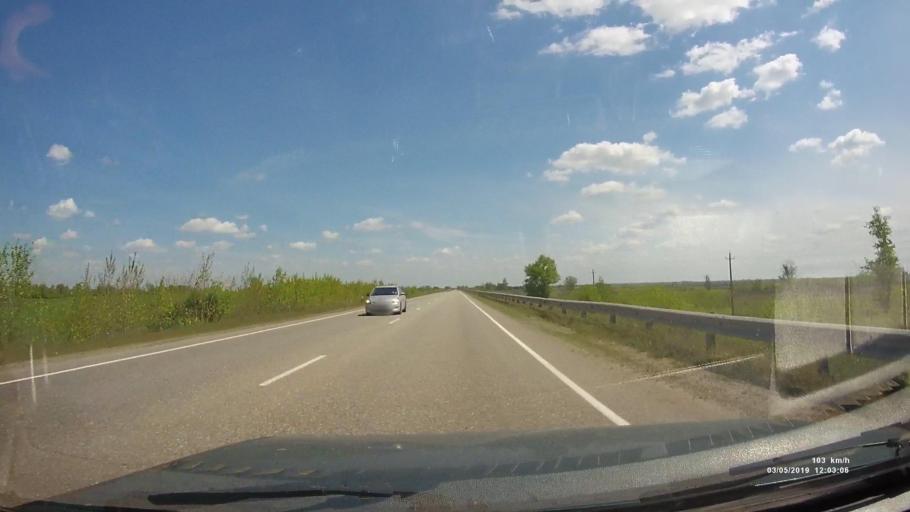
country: RU
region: Rostov
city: Bagayevskaya
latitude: 47.2732
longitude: 40.3826
